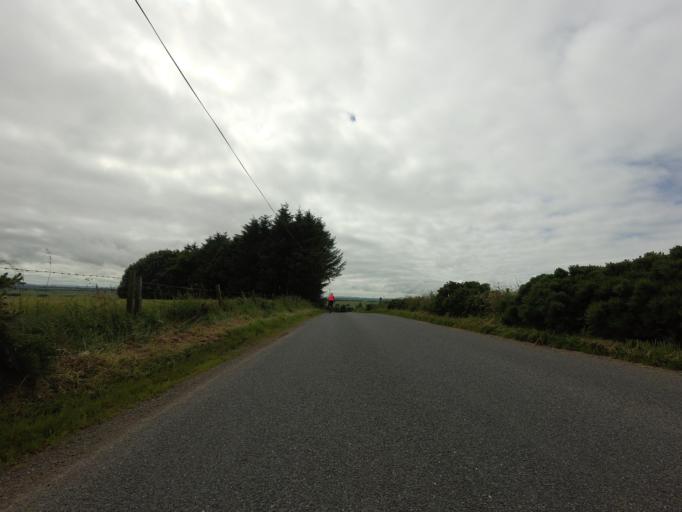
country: GB
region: Scotland
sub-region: Aberdeenshire
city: Rosehearty
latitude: 57.5437
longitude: -2.2448
